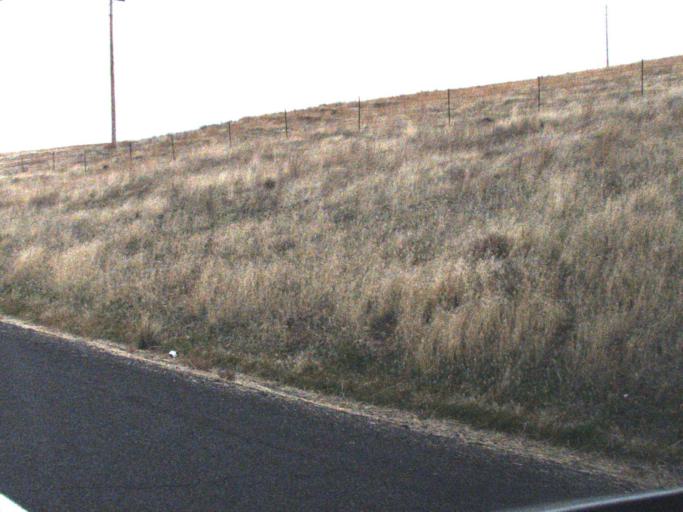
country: US
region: Washington
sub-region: Columbia County
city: Dayton
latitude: 46.7694
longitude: -117.9691
